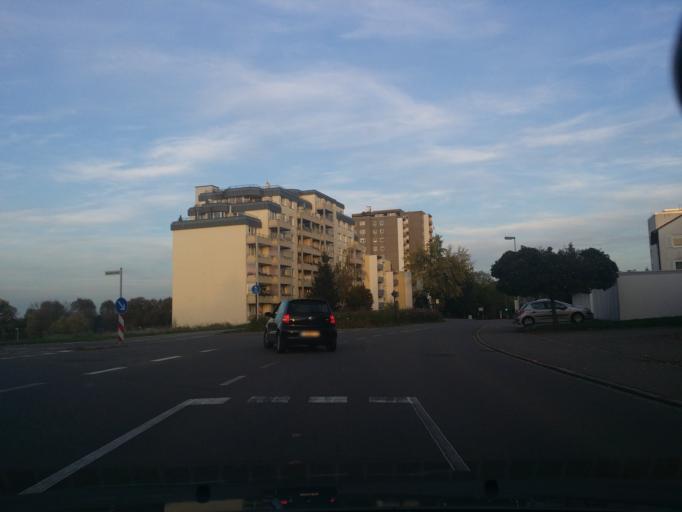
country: DE
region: Baden-Wuerttemberg
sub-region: Tuebingen Region
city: Ofterdingen
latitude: 48.4040
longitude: 9.0339
